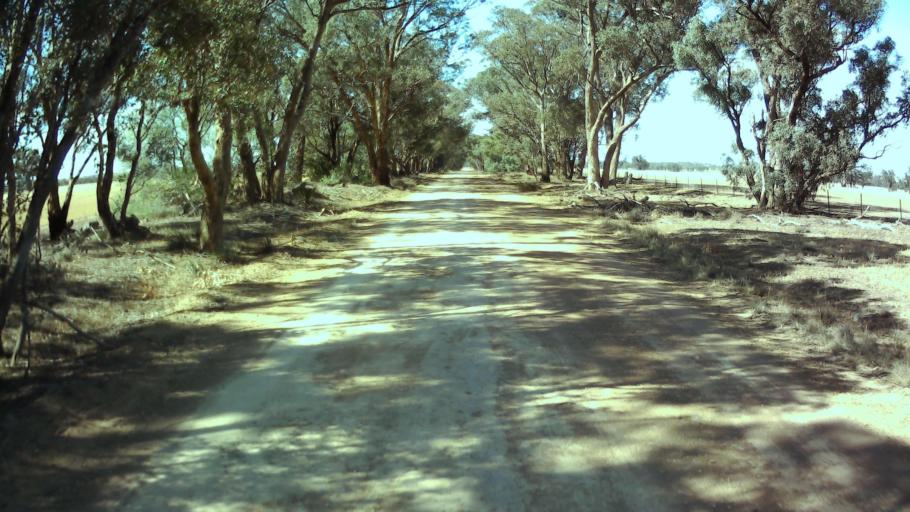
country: AU
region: New South Wales
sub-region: Weddin
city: Grenfell
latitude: -34.0488
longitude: 148.3143
